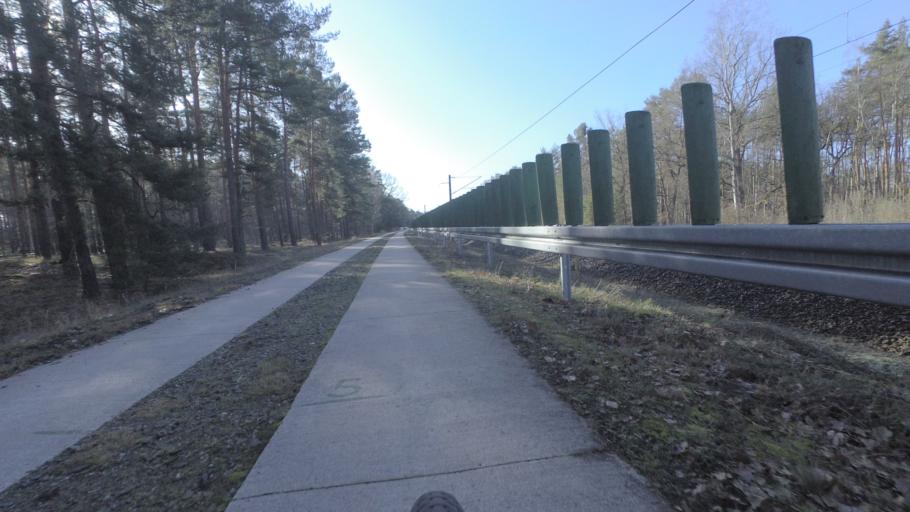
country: DE
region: Brandenburg
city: Luckenwalde
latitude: 52.1354
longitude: 13.2172
